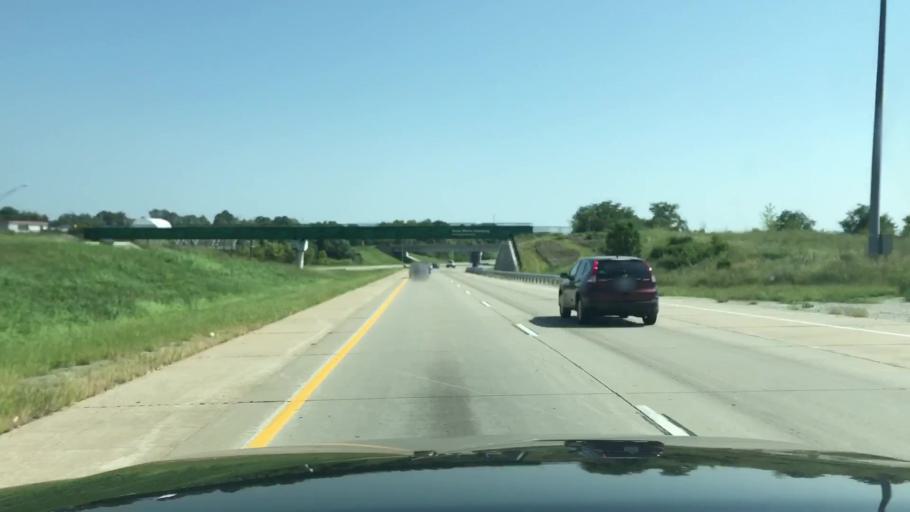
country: US
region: Missouri
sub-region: Saint Charles County
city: Saint Charles
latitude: 38.7548
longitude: -90.5462
